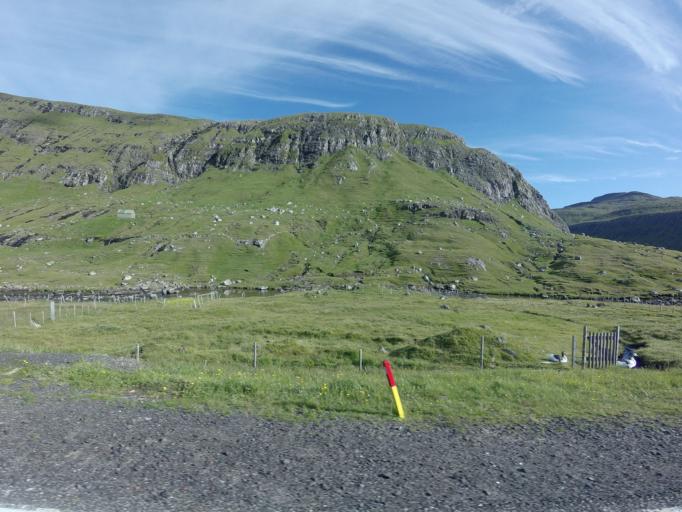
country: FO
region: Streymoy
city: Kollafjordhur
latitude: 62.1256
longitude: -7.0328
